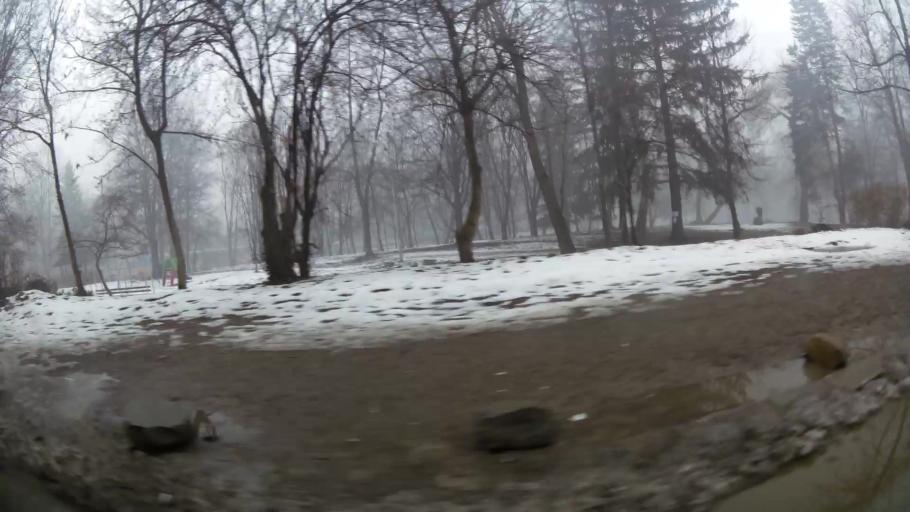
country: BG
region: Sofia-Capital
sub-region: Stolichna Obshtina
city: Sofia
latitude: 42.6602
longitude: 23.2491
